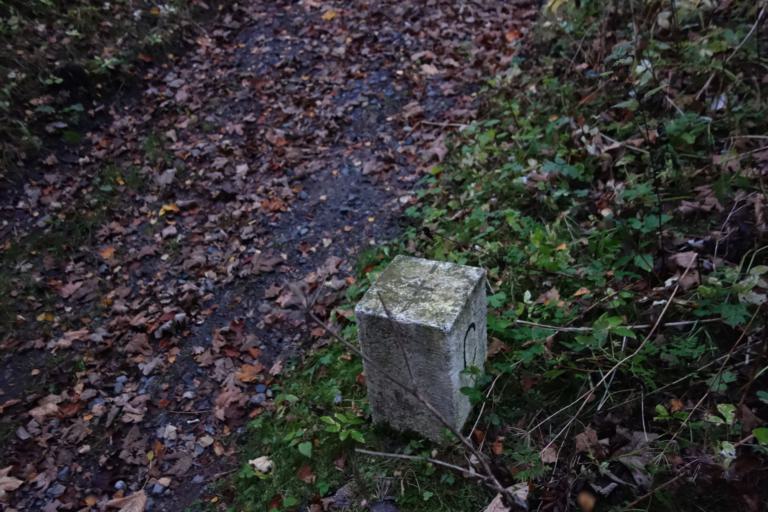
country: DE
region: Saxony
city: Johstadt
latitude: 50.5037
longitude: 13.1034
